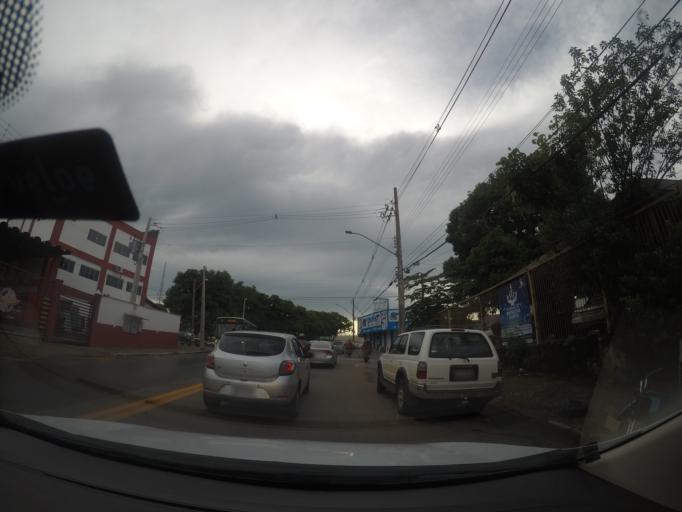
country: BR
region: Goias
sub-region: Goiania
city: Goiania
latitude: -16.6667
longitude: -49.3000
